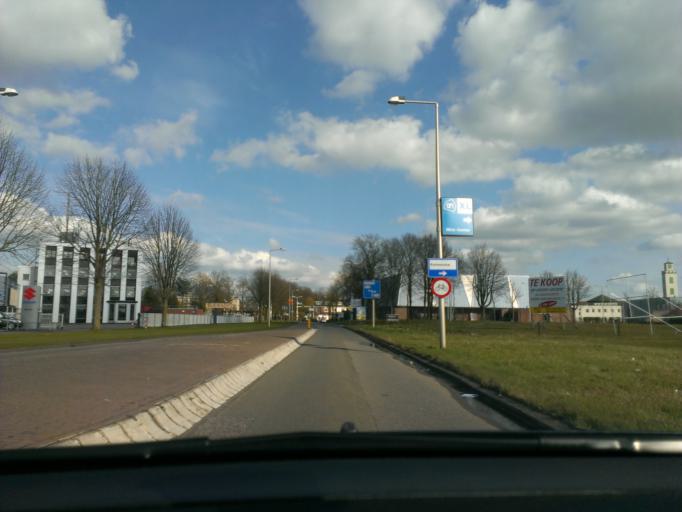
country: NL
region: Overijssel
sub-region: Gemeente Enschede
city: Enschede
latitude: 52.2183
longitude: 6.8703
